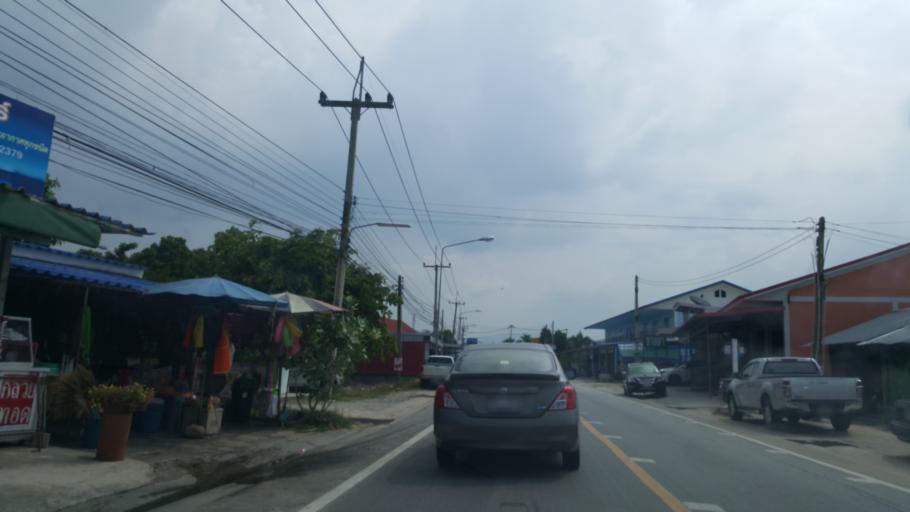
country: TH
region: Chon Buri
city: Si Racha
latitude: 13.2056
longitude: 101.0138
